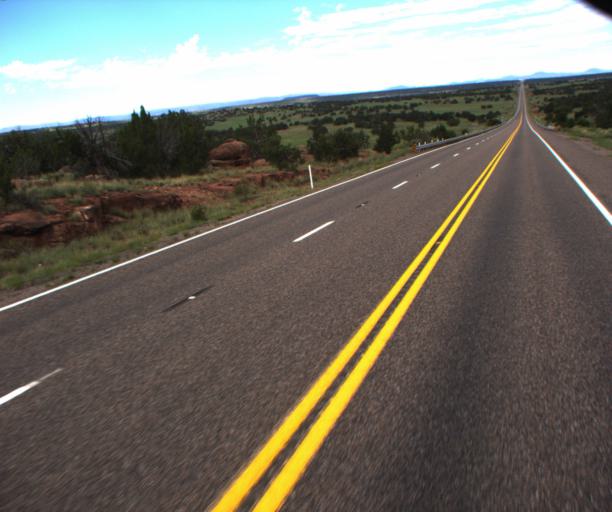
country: US
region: Arizona
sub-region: Apache County
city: Springerville
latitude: 34.1577
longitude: -109.1113
